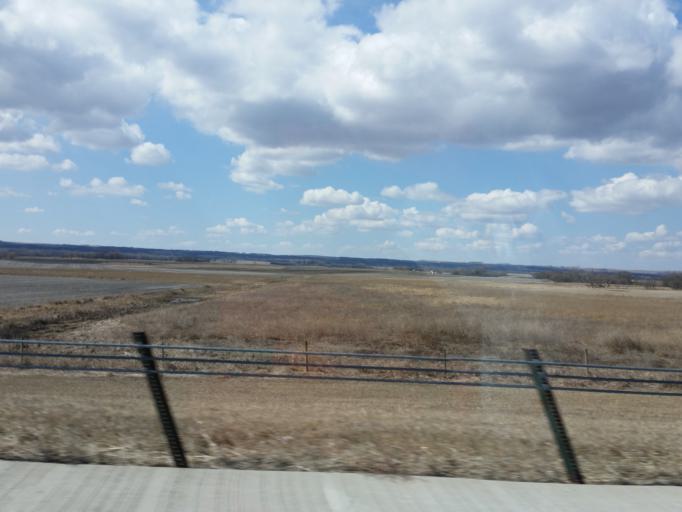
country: US
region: South Dakota
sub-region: Roberts County
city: Sisseton
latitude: 45.5705
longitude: -96.9897
